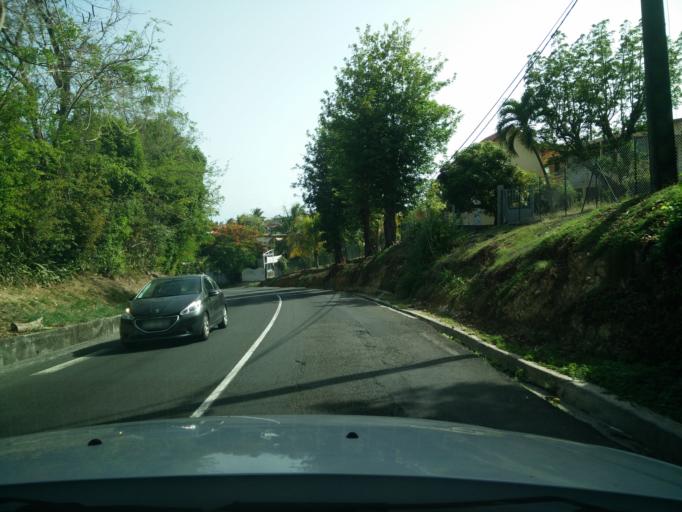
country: GP
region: Guadeloupe
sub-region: Guadeloupe
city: Le Gosier
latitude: 16.2117
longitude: -61.4410
